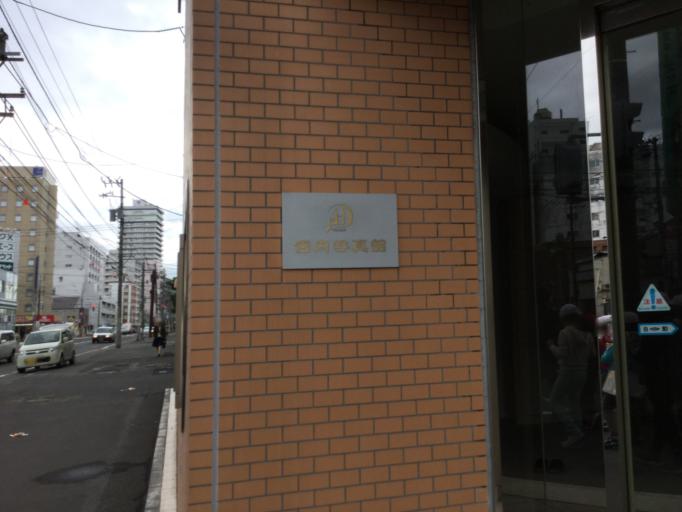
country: JP
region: Hokkaido
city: Sapporo
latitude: 43.0539
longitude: 141.3487
